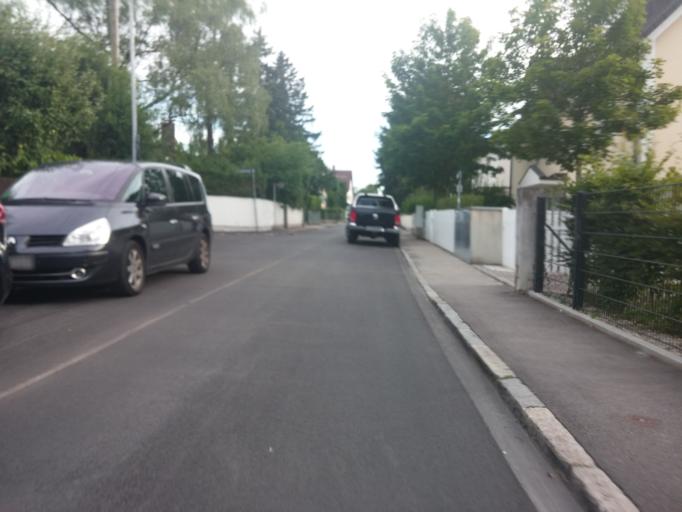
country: DE
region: Bavaria
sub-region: Upper Bavaria
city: Haar
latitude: 48.1136
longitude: 11.7051
